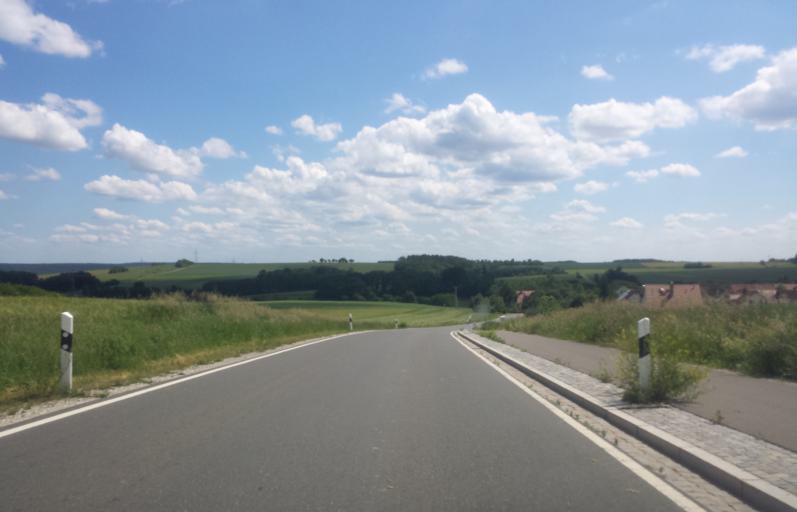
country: DE
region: Bavaria
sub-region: Upper Franconia
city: Hallerndorf
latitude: 49.7825
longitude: 10.9572
